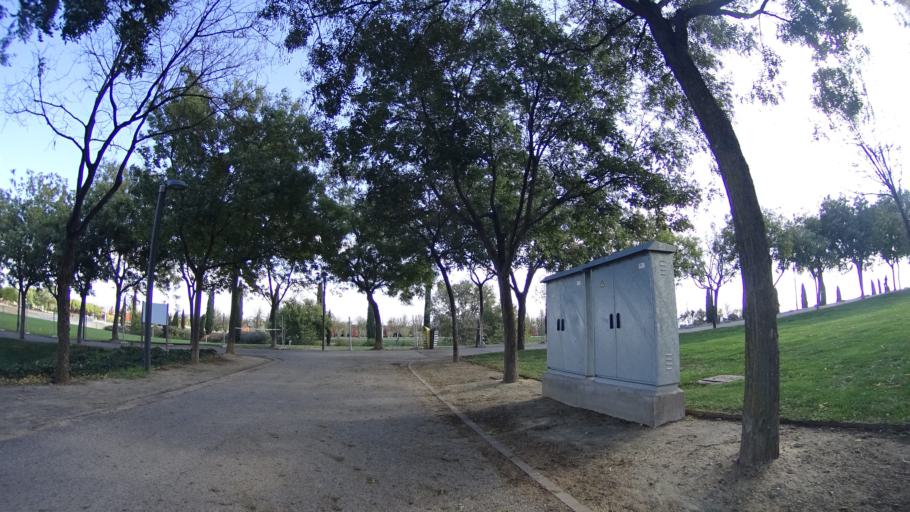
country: ES
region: Madrid
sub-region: Provincia de Madrid
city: San Blas
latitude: 40.4622
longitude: -3.6121
